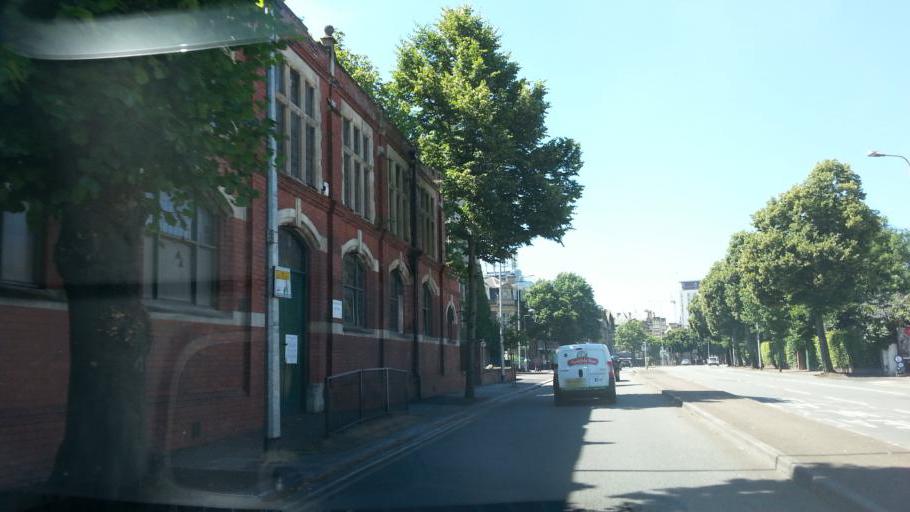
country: GB
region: Wales
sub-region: Cardiff
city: Cardiff
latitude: 51.4872
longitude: -3.1600
